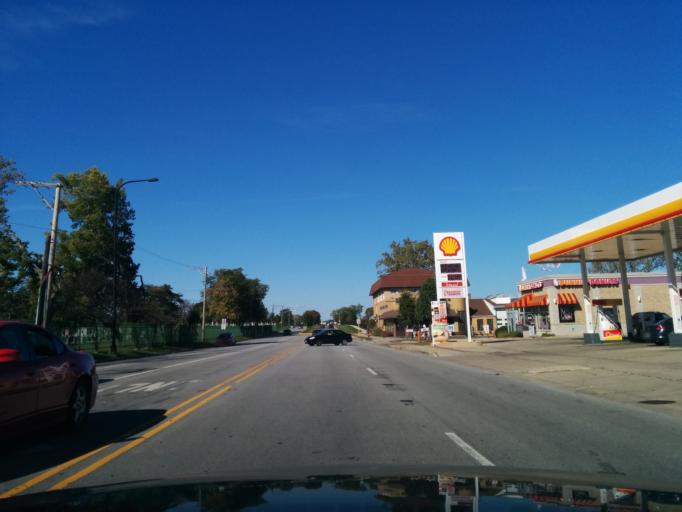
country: US
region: Illinois
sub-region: Cook County
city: Hillside
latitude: 41.8629
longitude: -87.9020
